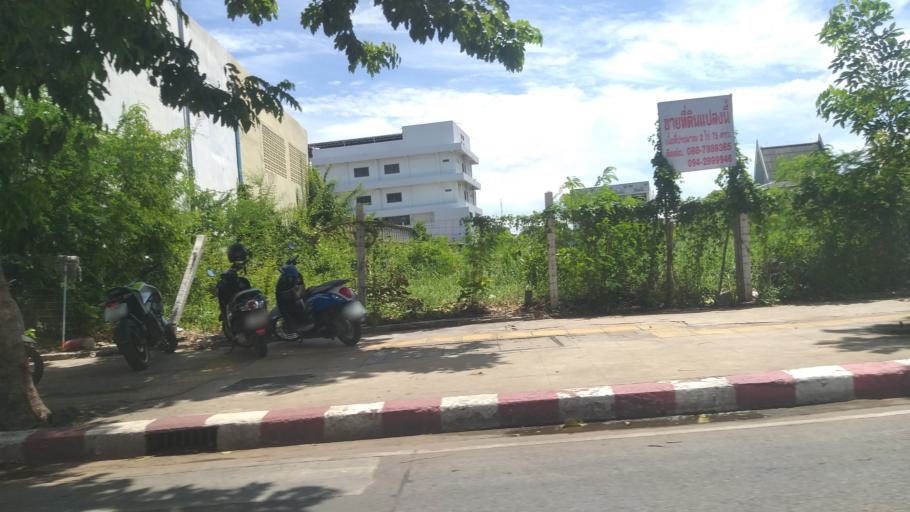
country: TH
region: Khon Kaen
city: Khon Kaen
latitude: 16.4313
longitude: 102.8296
